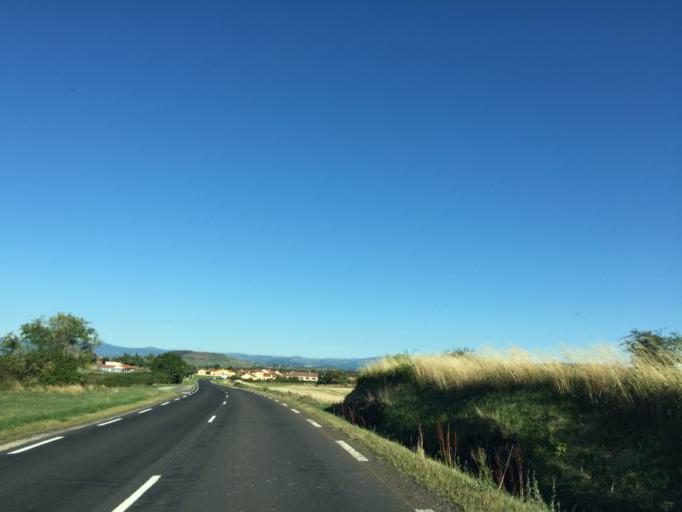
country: FR
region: Auvergne
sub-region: Departement de la Haute-Loire
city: Bains
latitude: 45.0099
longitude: 3.7914
